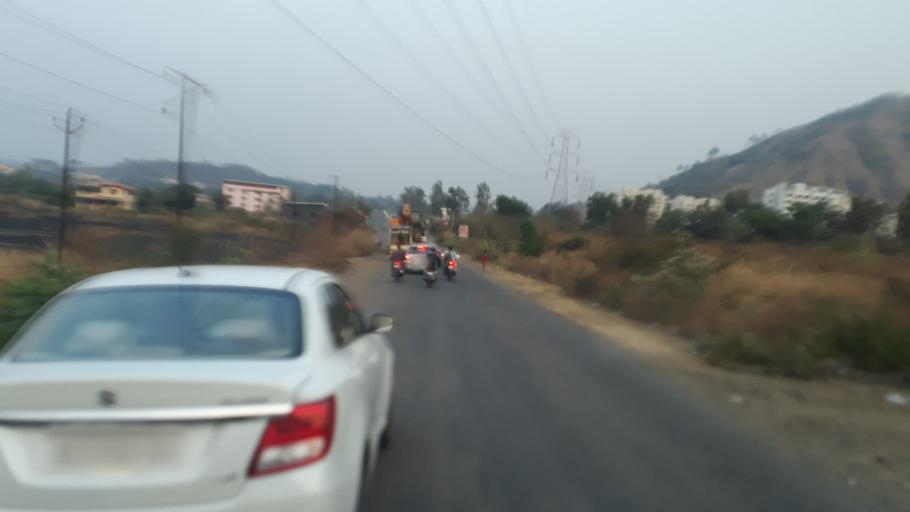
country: IN
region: Maharashtra
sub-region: Raigarh
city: Neral
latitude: 19.0179
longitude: 73.3131
